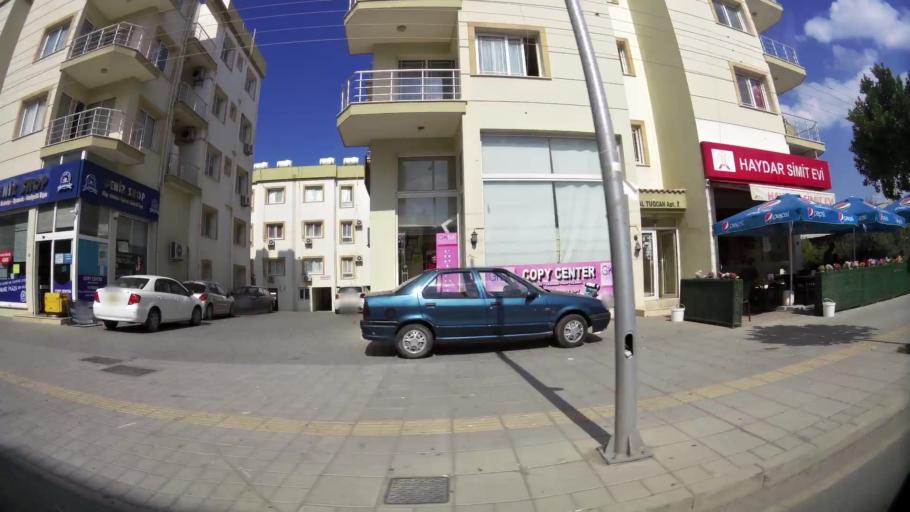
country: CY
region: Lefkosia
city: Nicosia
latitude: 35.2104
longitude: 33.3141
